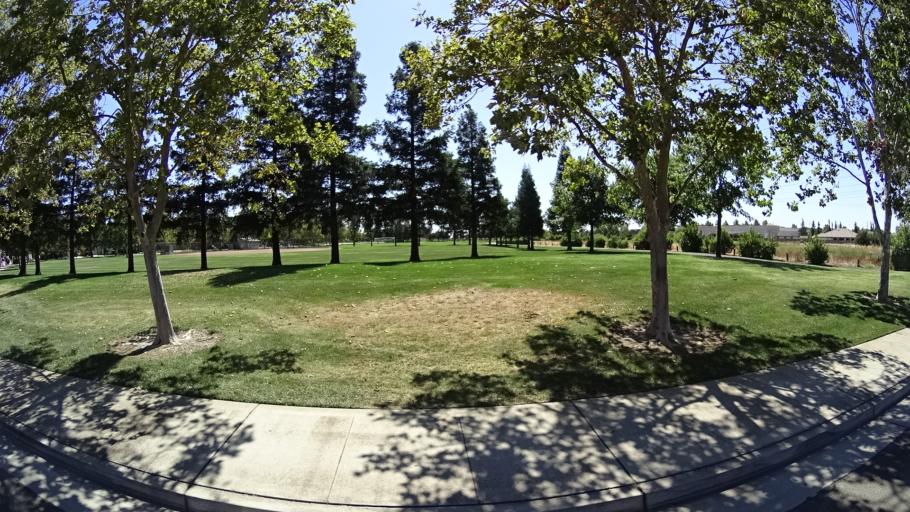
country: US
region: California
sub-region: Sacramento County
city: Elk Grove
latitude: 38.4117
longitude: -121.3494
